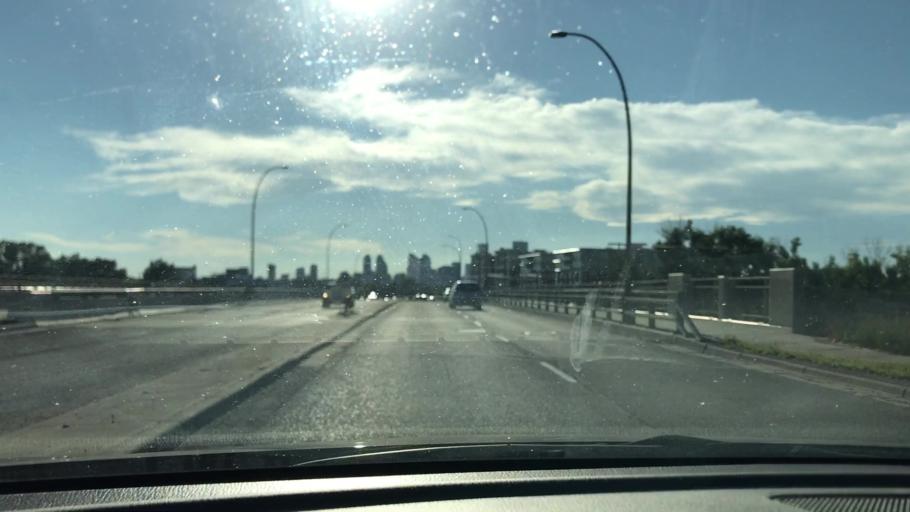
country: CA
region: Alberta
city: Calgary
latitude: 51.0372
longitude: -114.0119
